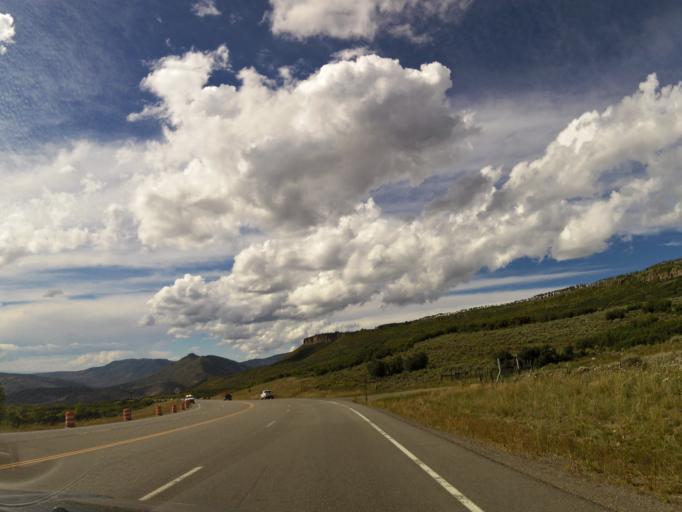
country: US
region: Colorado
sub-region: Hinsdale County
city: Lake City
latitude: 38.3870
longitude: -107.4343
